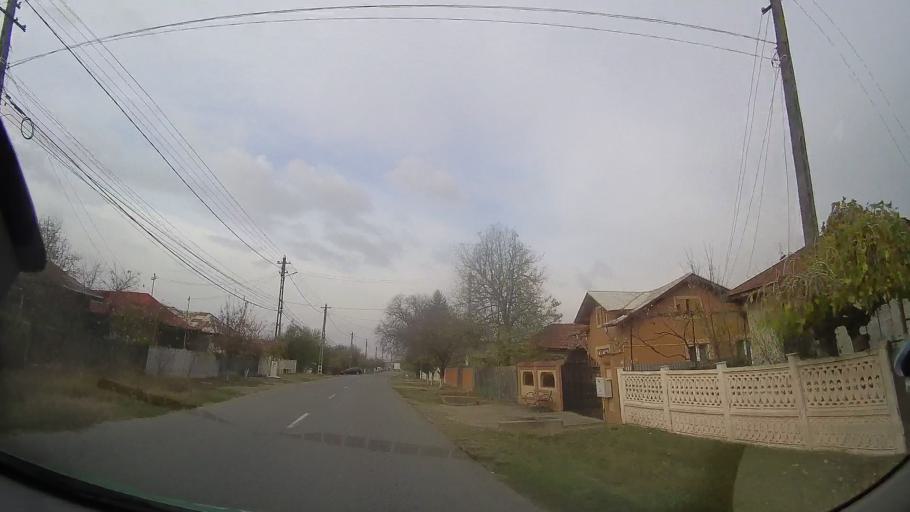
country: RO
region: Prahova
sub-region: Comuna Gorgota
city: Potigrafu
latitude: 44.7790
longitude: 26.1033
